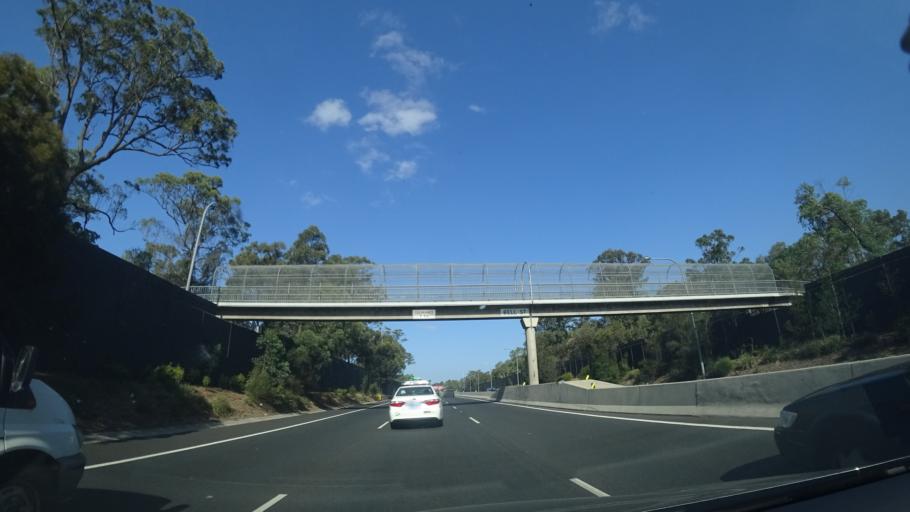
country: AU
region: New South Wales
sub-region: Bankstown
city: Padstow
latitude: -33.9418
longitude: 151.0471
